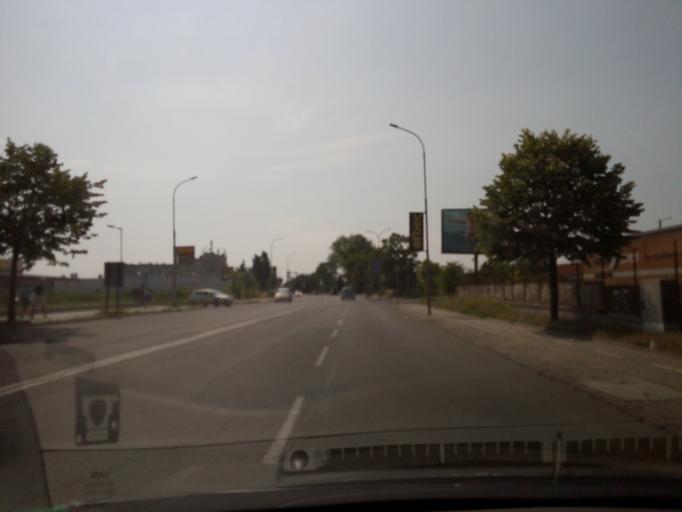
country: BG
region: Burgas
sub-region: Obshtina Pomorie
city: Pomorie
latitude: 42.5662
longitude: 27.6209
